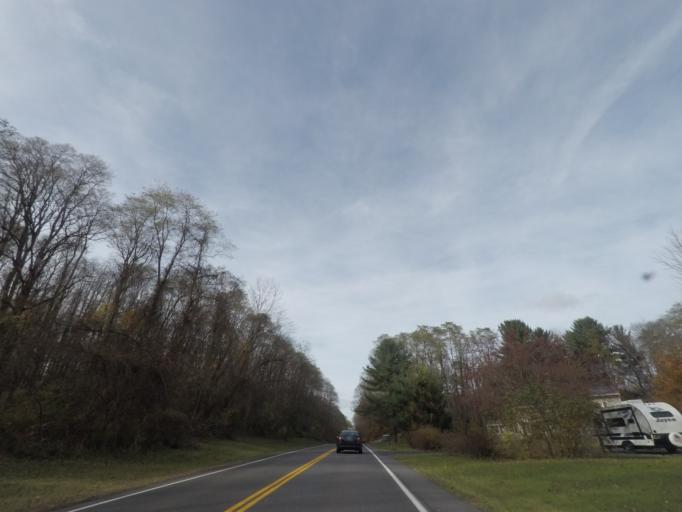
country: US
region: New York
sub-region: Albany County
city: Westmere
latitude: 42.7275
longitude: -73.8971
